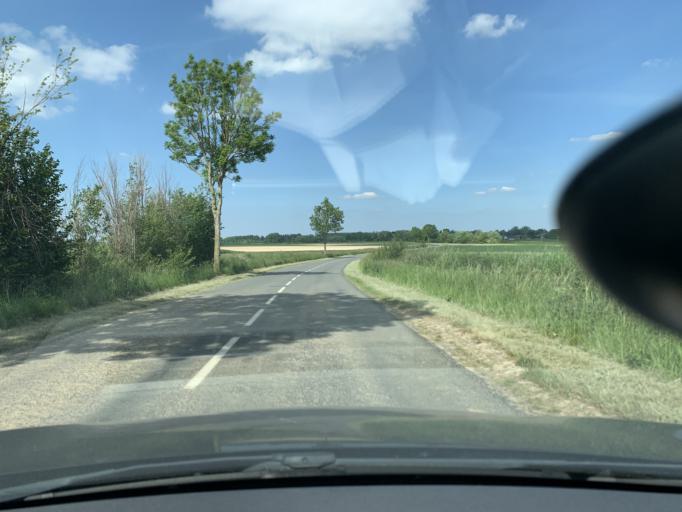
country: FR
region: Nord-Pas-de-Calais
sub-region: Departement du Pas-de-Calais
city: Marquion
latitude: 50.2290
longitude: 3.0846
